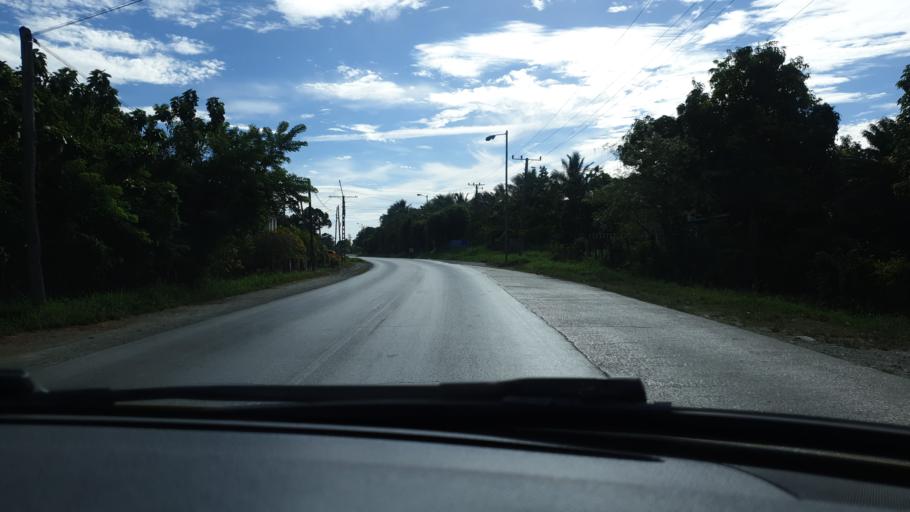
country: CU
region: Villa Clara
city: Santa Clara
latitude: 22.4163
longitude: -79.9444
